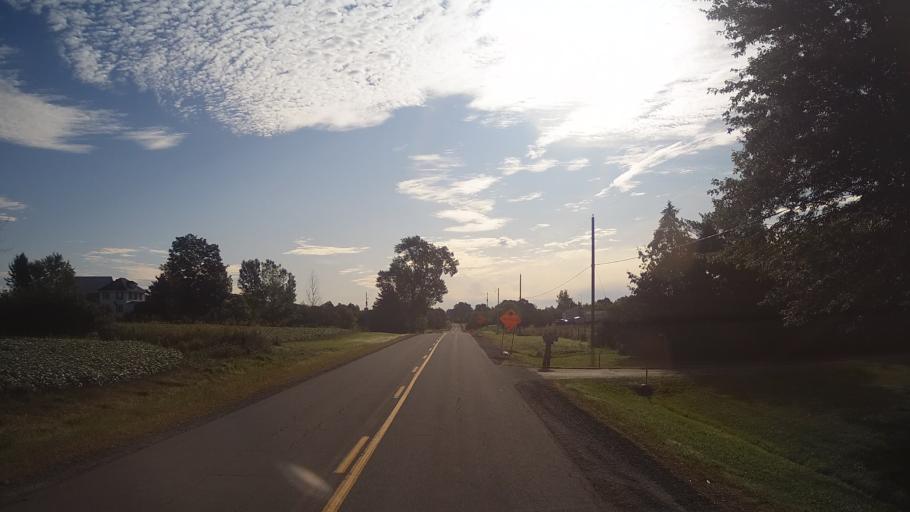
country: CA
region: Ontario
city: Gananoque
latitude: 44.4001
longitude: -76.1043
